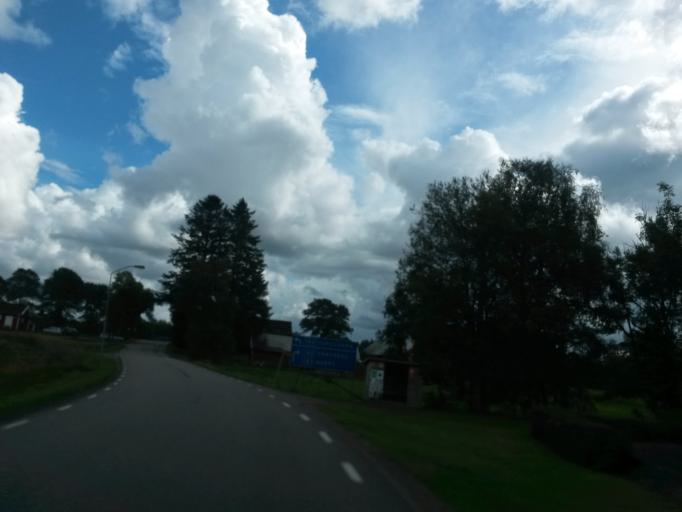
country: SE
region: Vaestra Goetaland
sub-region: Herrljunga Kommun
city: Herrljunga
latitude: 57.9921
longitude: 13.0201
